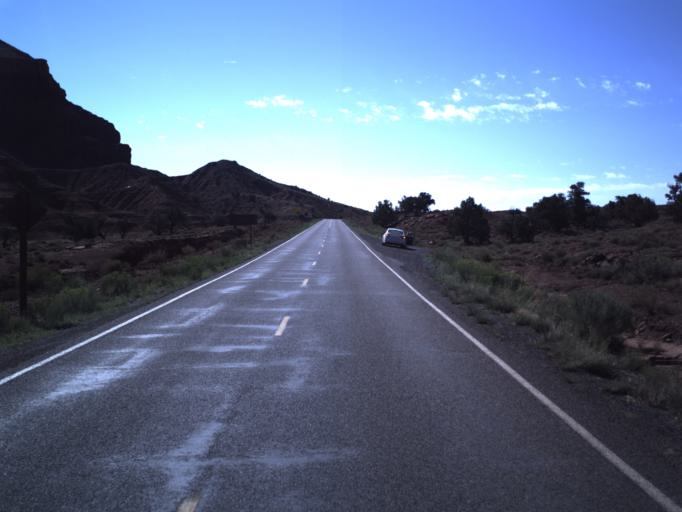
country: US
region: Utah
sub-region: Wayne County
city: Loa
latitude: 38.3148
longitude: -111.3040
